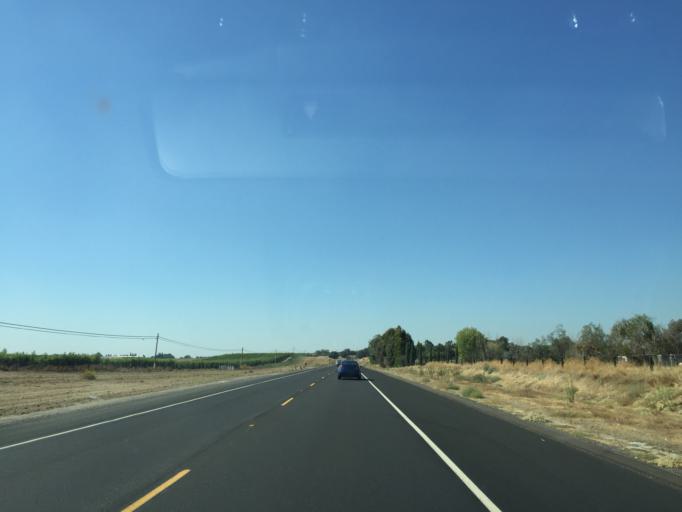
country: US
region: California
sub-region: Stanislaus County
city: East Oakdale
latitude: 37.7794
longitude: -120.7638
